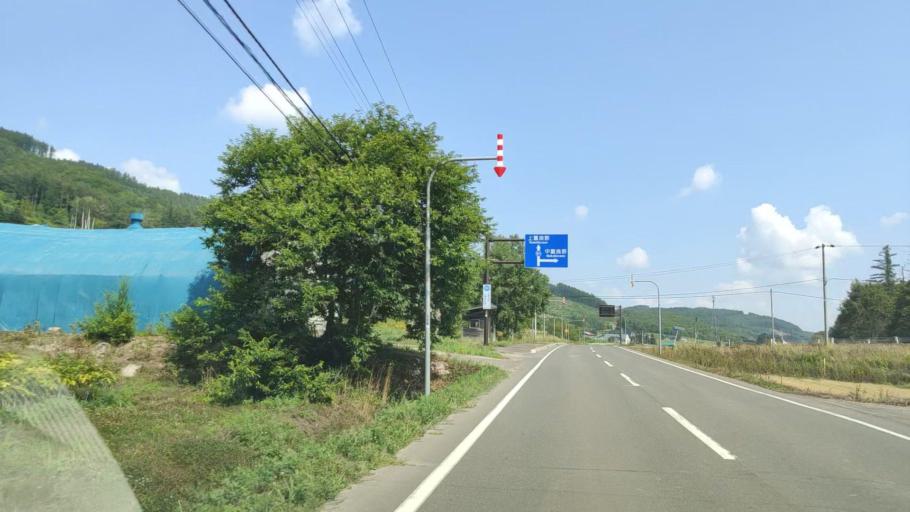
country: JP
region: Hokkaido
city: Shimo-furano
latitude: 43.4341
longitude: 142.4096
